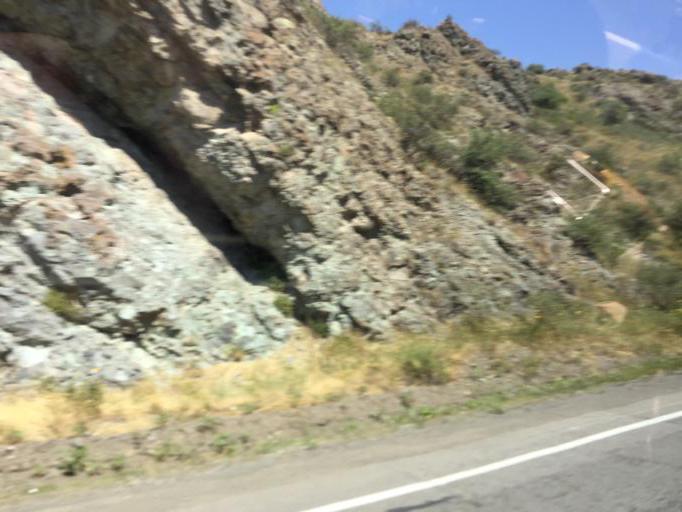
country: AM
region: Vayots' Dzori Marz
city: Jermuk
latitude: 39.7169
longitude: 45.6285
